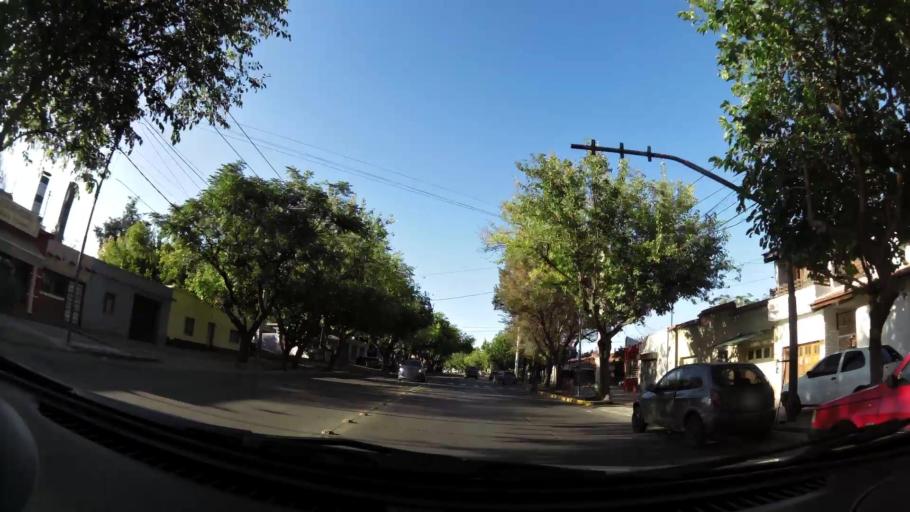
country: AR
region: Mendoza
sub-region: Departamento de Godoy Cruz
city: Godoy Cruz
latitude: -32.9378
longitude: -68.8503
